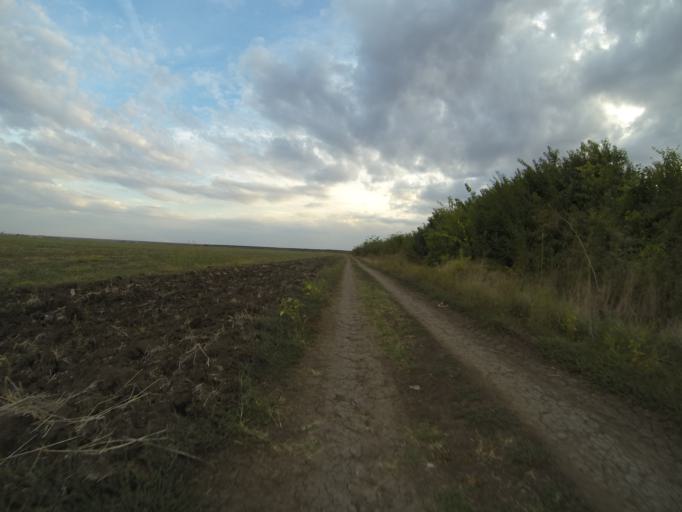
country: RO
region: Dolj
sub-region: Comuna Ceratu
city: Ceratu
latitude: 44.1047
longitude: 23.6930
